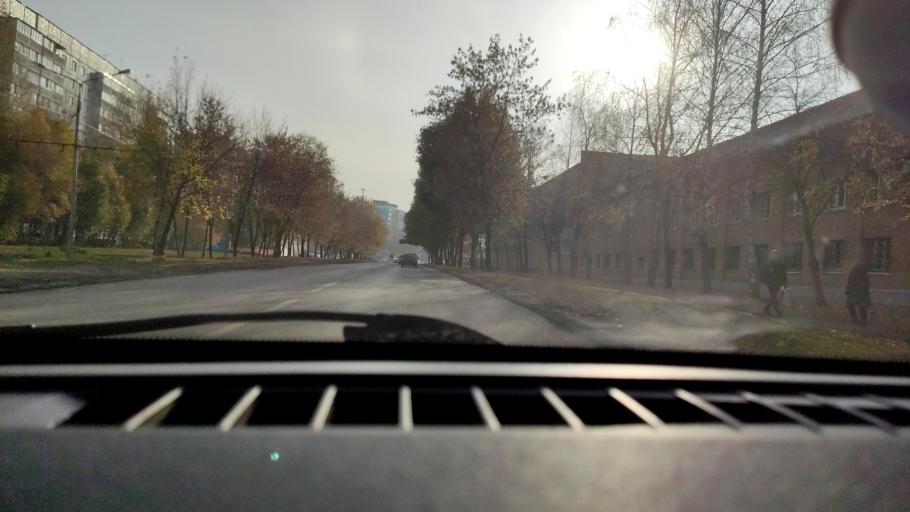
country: RU
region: Samara
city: Samara
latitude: 53.2448
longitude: 50.2063
